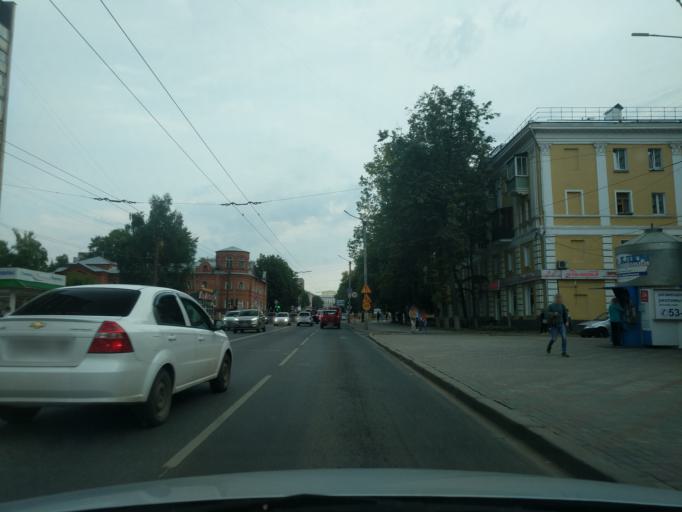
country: RU
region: Kirov
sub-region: Kirovo-Chepetskiy Rayon
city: Kirov
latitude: 58.6125
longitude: 49.6672
